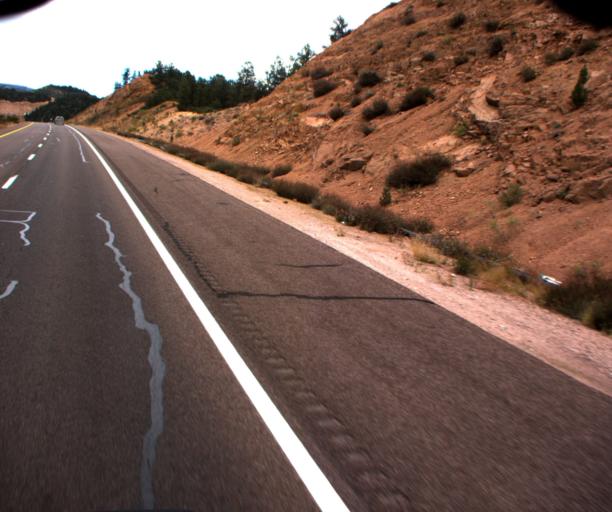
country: US
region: Arizona
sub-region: Gila County
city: Star Valley
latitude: 34.2721
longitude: -111.1785
